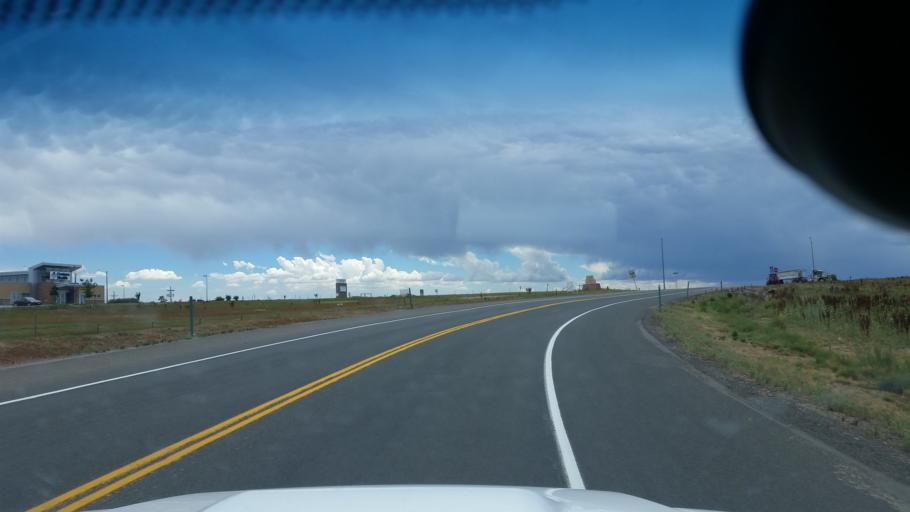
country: US
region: Colorado
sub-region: Weld County
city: Dacono
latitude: 40.0457
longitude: -104.9768
